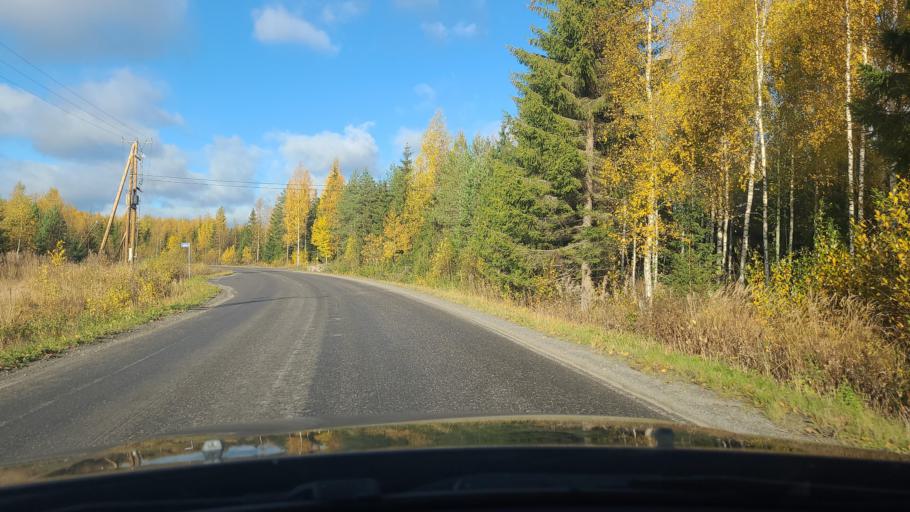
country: FI
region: Southern Savonia
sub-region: Pieksaemaeki
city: Juva
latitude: 61.8820
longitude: 27.7551
